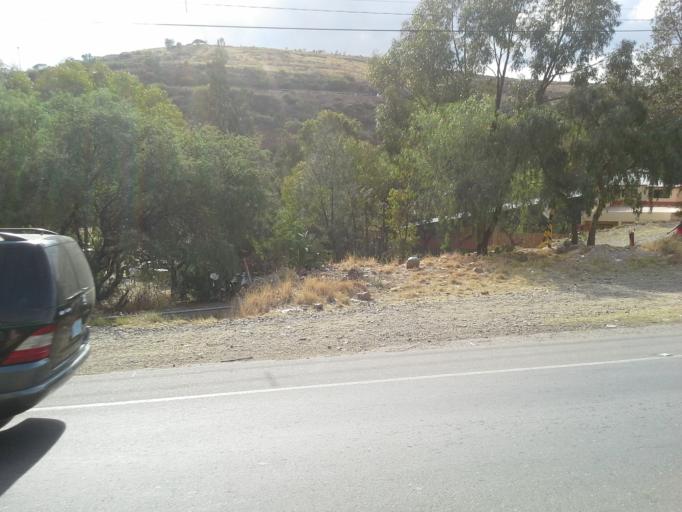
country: BO
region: Cochabamba
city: Tarata
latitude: -17.5274
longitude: -66.0848
